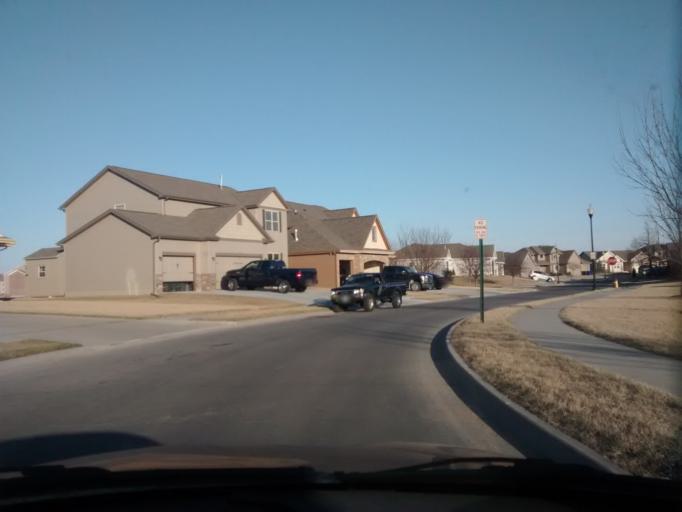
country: US
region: Nebraska
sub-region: Sarpy County
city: Offutt Air Force Base
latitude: 41.1449
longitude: -95.9792
